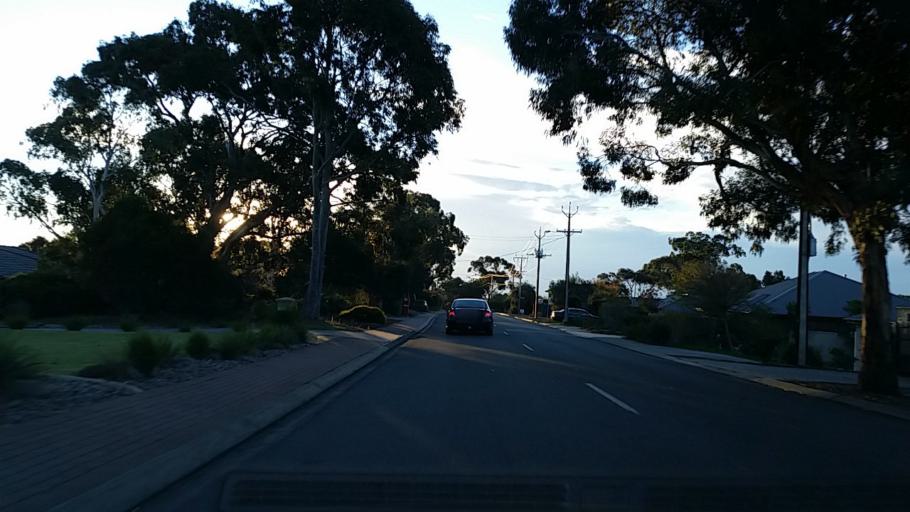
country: AU
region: South Australia
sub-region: Onkaparinga
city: Craigburn Farm
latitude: -35.0651
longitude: 138.6096
